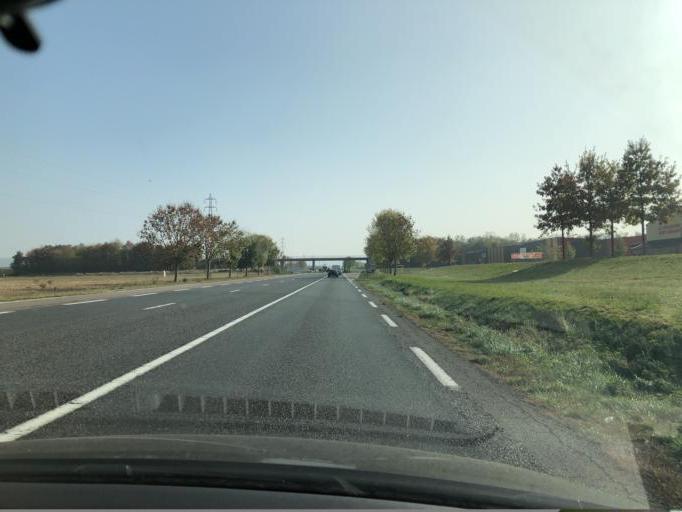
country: FR
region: Bourgogne
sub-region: Departement de l'Yonne
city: Saint-Clement
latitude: 48.2250
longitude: 3.2851
